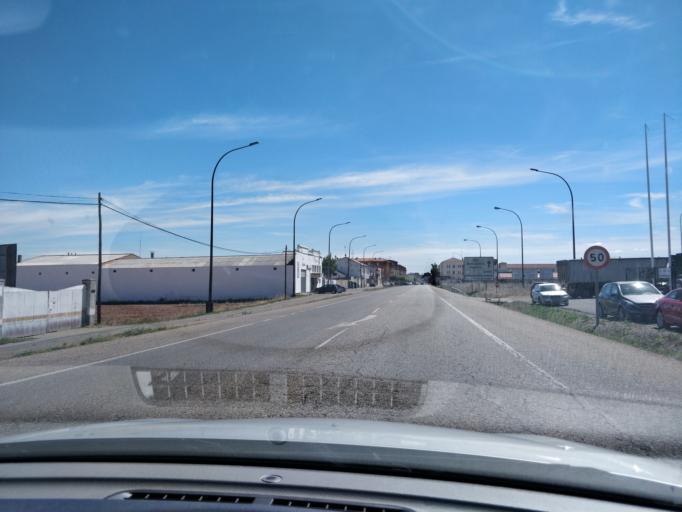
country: ES
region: Castille and Leon
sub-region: Provincia de Leon
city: Astorga
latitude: 42.4641
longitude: -6.0722
